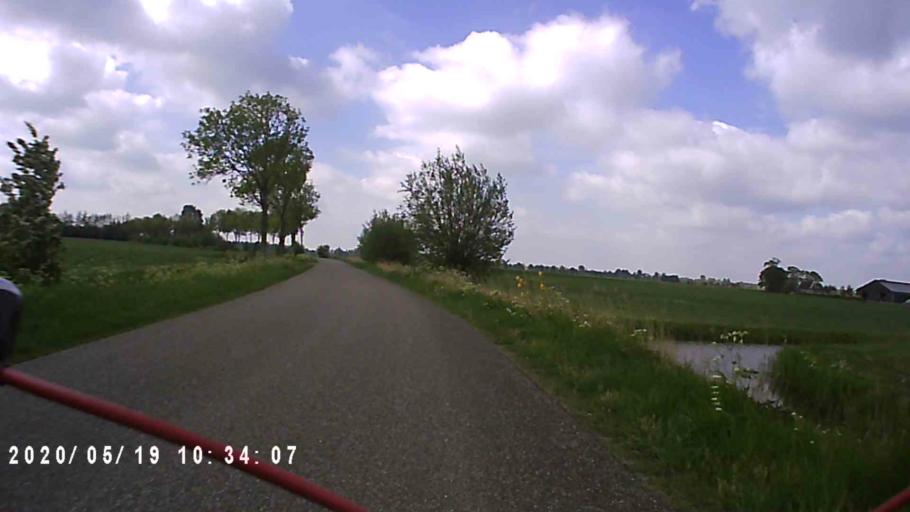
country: NL
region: Friesland
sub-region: Gemeente Kollumerland en Nieuwkruisland
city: Kollum
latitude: 53.2863
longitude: 6.1856
